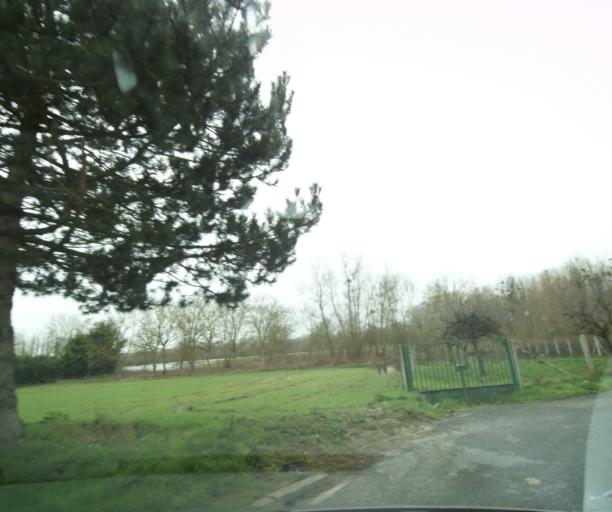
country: FR
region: Picardie
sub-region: Departement de l'Oise
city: Noyon
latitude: 49.5694
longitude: 3.0204
